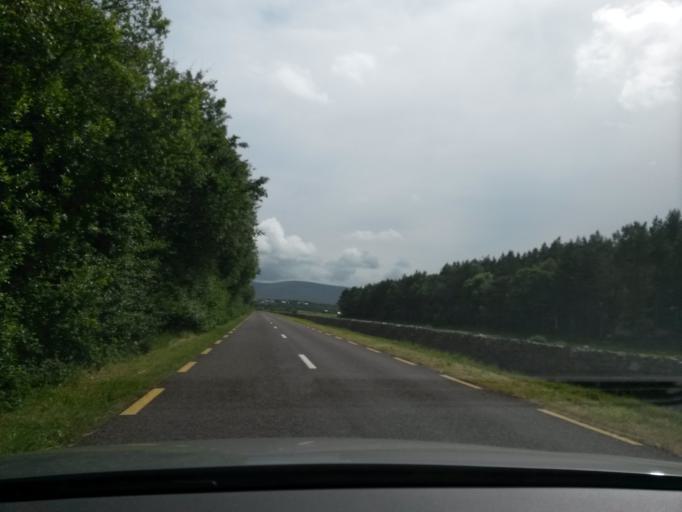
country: IE
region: Connaught
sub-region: County Leitrim
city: Kinlough
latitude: 54.4461
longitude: -8.4546
